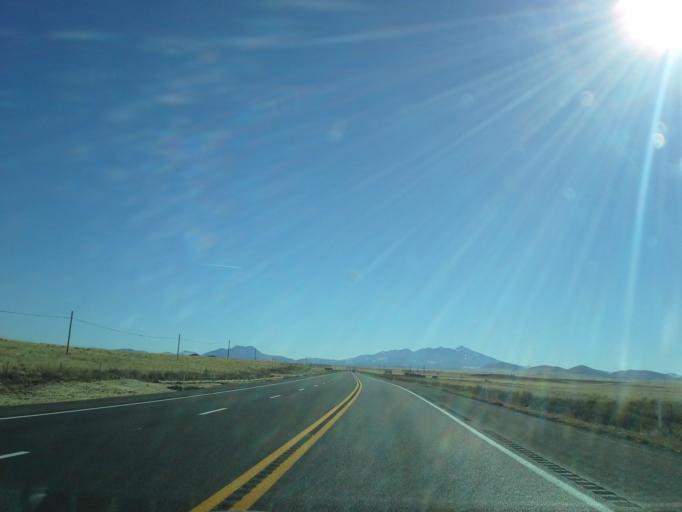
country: US
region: Arizona
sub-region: Coconino County
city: Flagstaff
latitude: 35.6904
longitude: -111.5045
